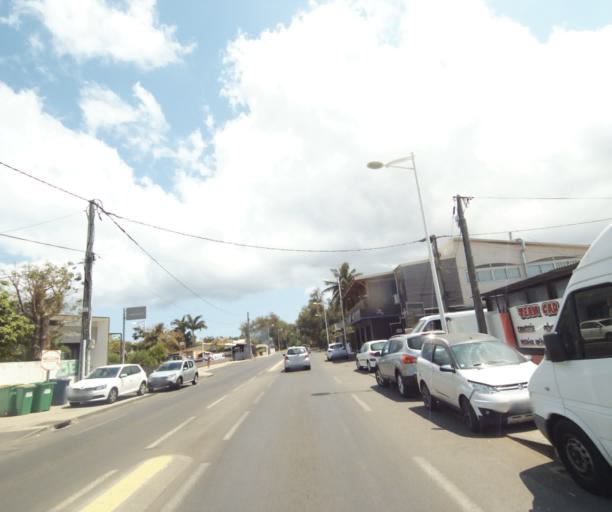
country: RE
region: Reunion
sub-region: Reunion
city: Trois-Bassins
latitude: -21.0812
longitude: 55.2301
